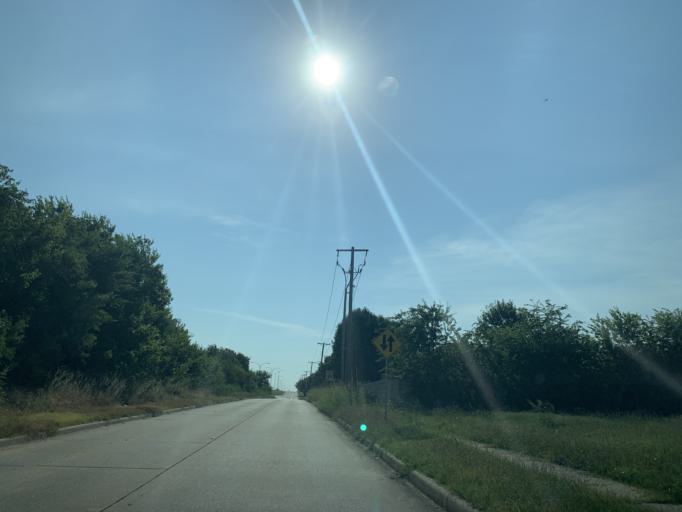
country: US
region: Texas
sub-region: Tarrant County
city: Blue Mound
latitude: 32.8856
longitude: -97.3066
